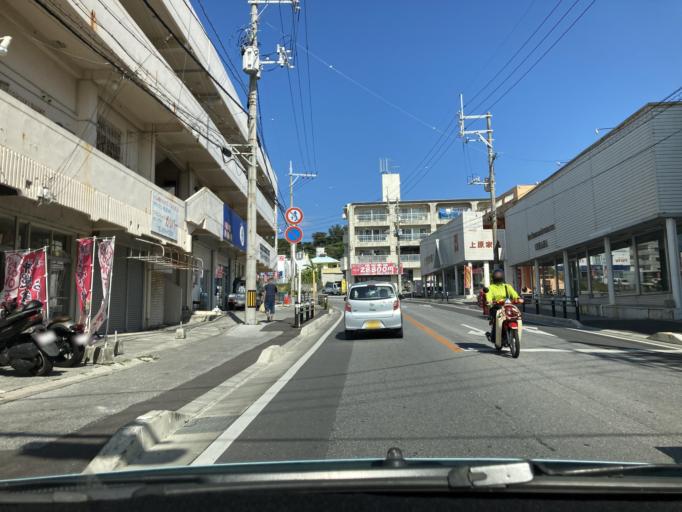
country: JP
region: Okinawa
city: Tomigusuku
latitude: 26.1793
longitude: 127.6647
